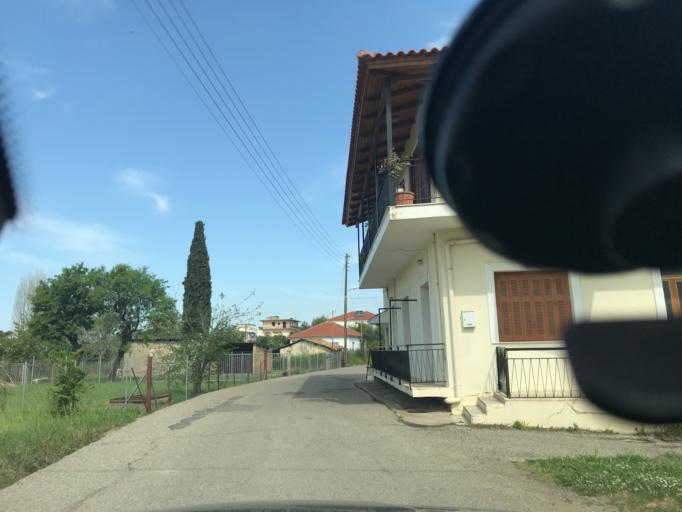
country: GR
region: West Greece
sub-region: Nomos Ileias
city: Pyrgos
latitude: 37.6778
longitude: 21.4395
